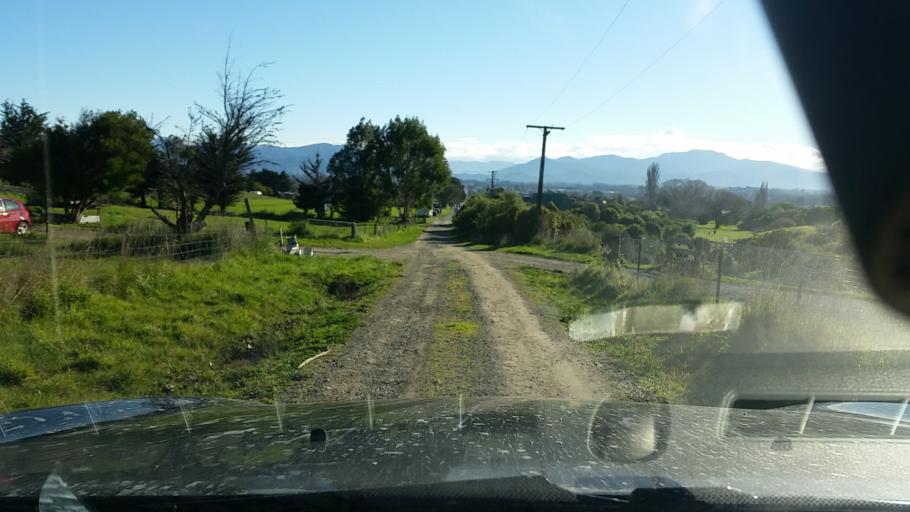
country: NZ
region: Marlborough
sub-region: Marlborough District
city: Blenheim
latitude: -41.5445
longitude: 173.9628
